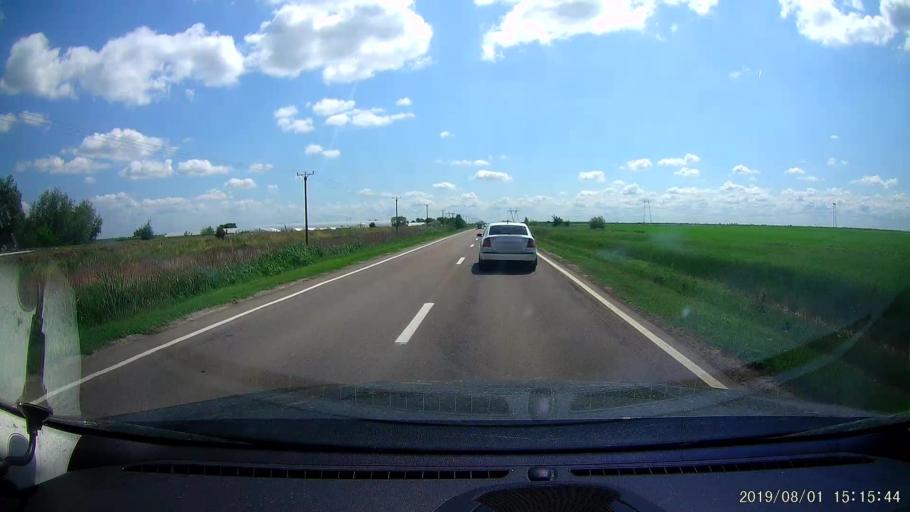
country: RO
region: Braila
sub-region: Comuna Tichilesti
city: Tichilesti
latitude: 45.1596
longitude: 27.8640
